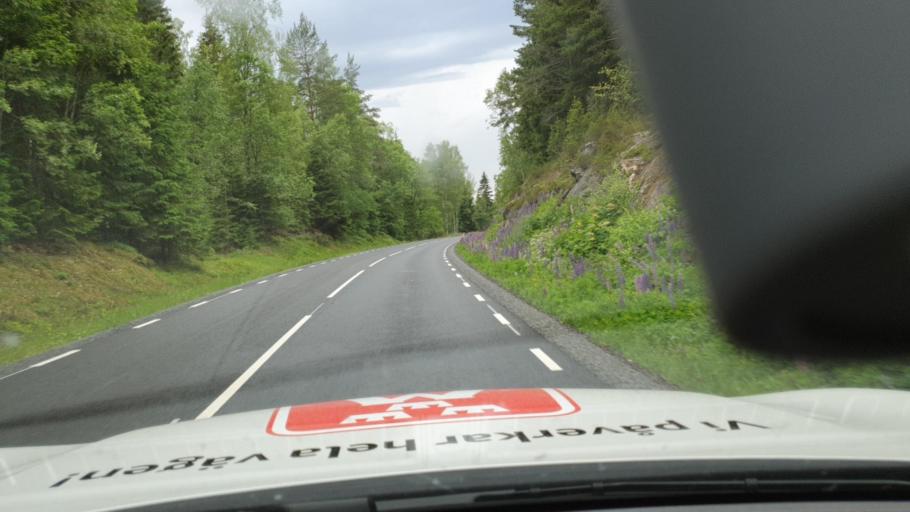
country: SE
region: OErebro
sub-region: Laxa Kommun
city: Laxa
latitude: 58.9005
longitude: 14.4738
